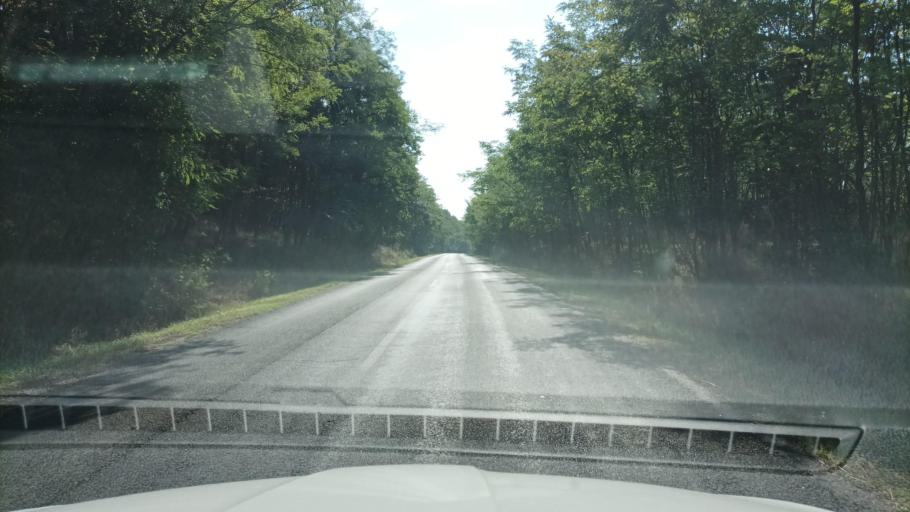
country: HU
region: Pest
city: Isaszeg
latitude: 47.5695
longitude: 19.4430
